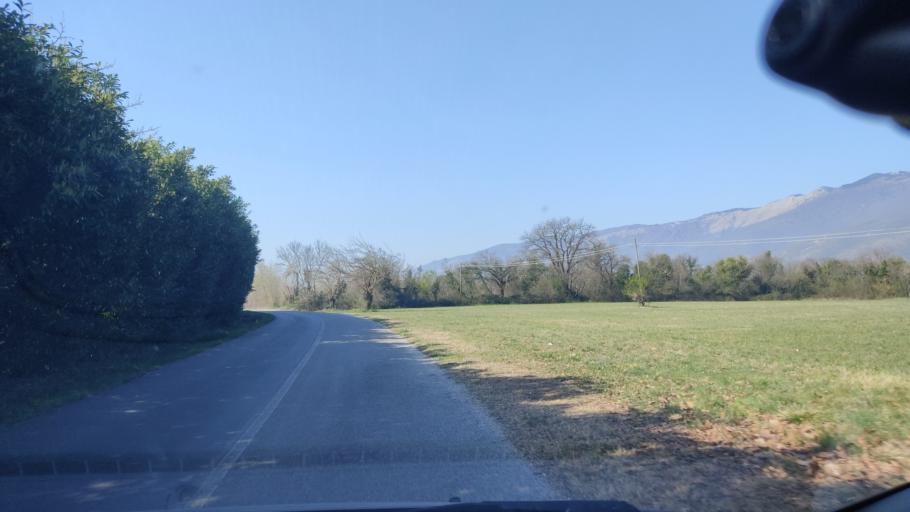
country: IT
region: Friuli Venezia Giulia
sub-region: Provincia di Pordenone
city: Budoia
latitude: 46.0517
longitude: 12.5518
